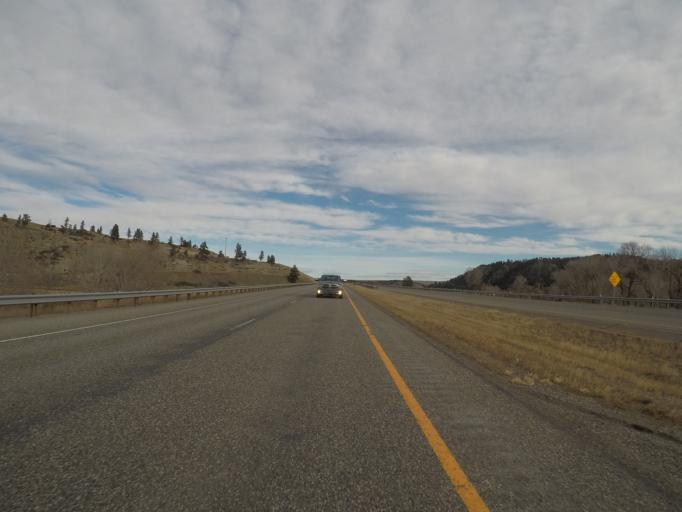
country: US
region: Montana
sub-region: Stillwater County
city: Absarokee
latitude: 45.6850
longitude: -109.4281
